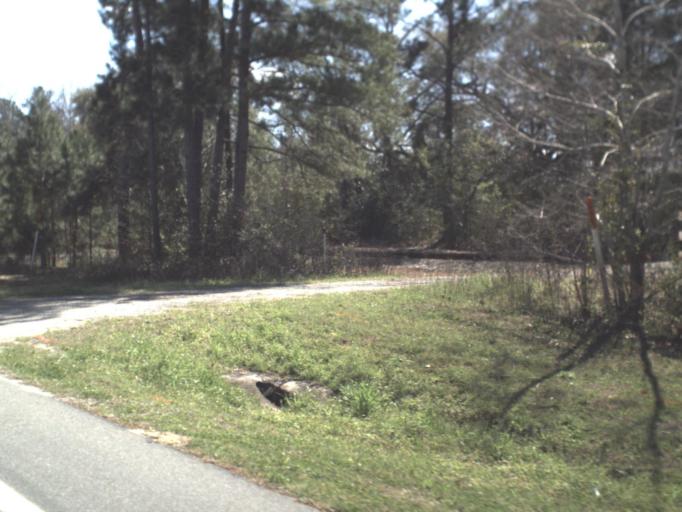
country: US
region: Florida
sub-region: Gadsden County
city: Gretna
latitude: 30.6271
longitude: -84.6692
